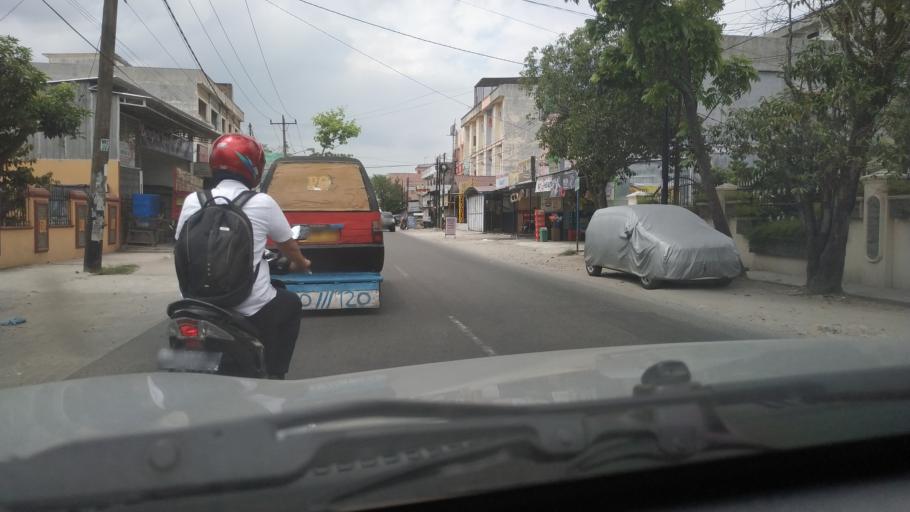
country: ID
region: North Sumatra
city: Sunggal
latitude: 3.5854
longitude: 98.6167
